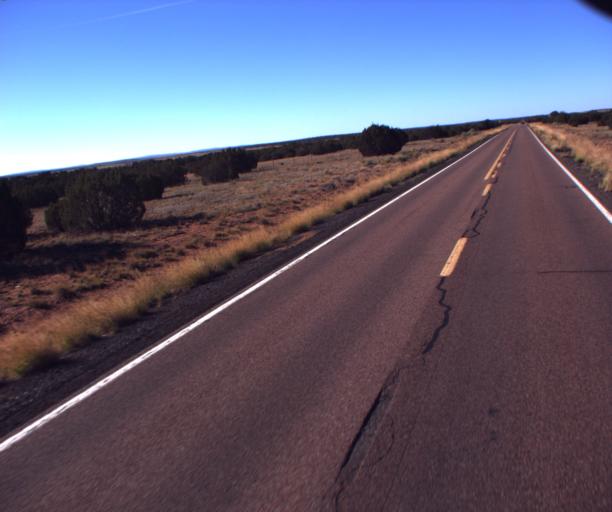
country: US
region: Arizona
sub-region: Navajo County
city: Heber-Overgaard
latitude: 34.5758
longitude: -110.4095
